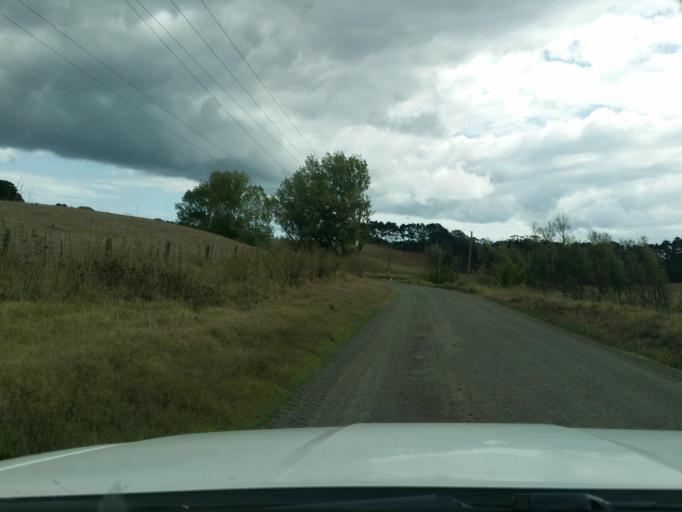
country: NZ
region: Auckland
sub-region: Auckland
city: Wellsford
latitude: -36.3290
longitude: 174.1506
